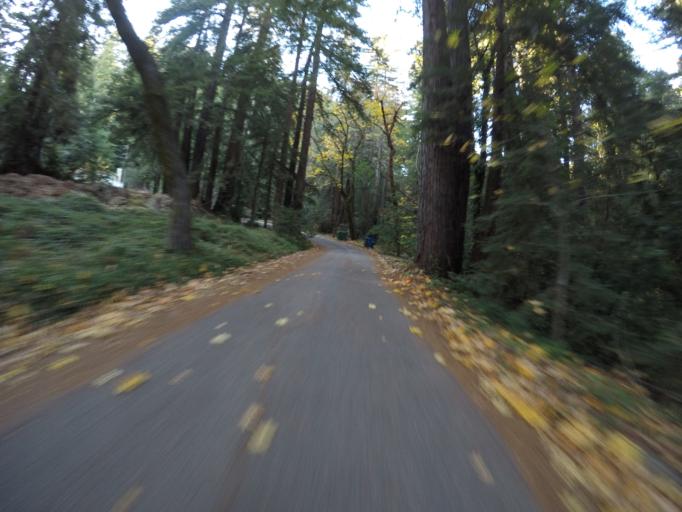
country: US
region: California
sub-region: Santa Cruz County
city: Scotts Valley
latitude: 37.0773
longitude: -121.9923
